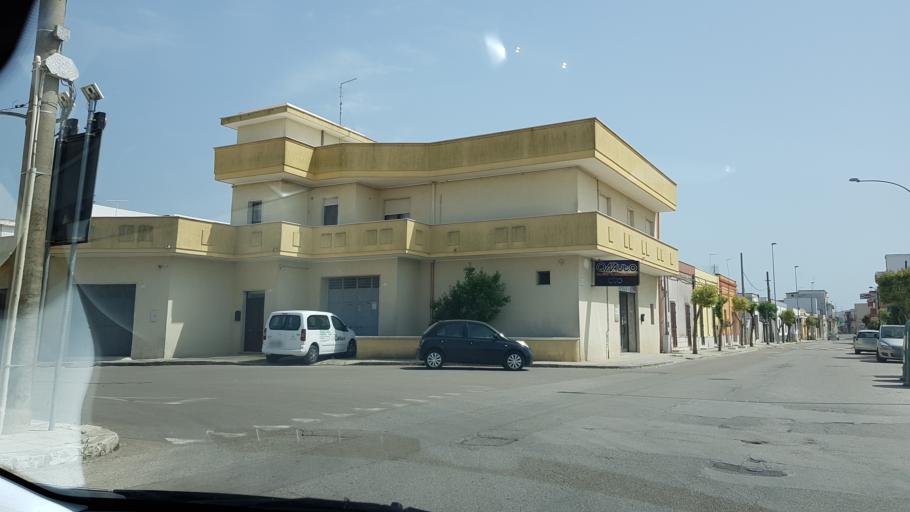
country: IT
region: Apulia
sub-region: Provincia di Brindisi
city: San Pancrazio Salentino
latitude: 40.4232
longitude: 17.8410
